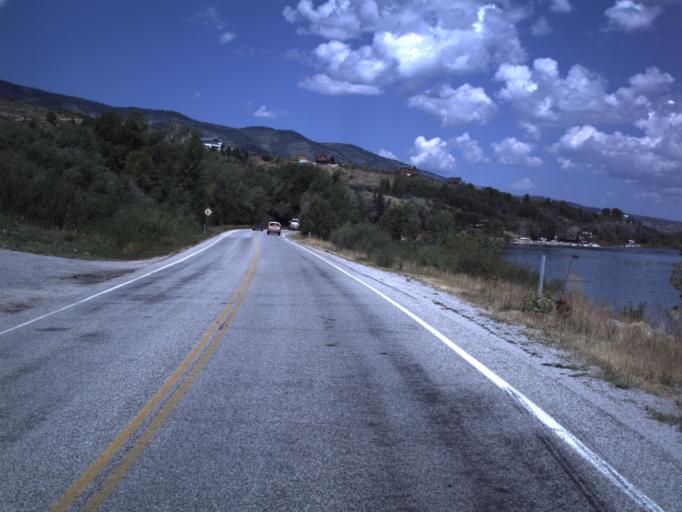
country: US
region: Idaho
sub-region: Bear Lake County
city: Paris
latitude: 41.9676
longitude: -111.4000
